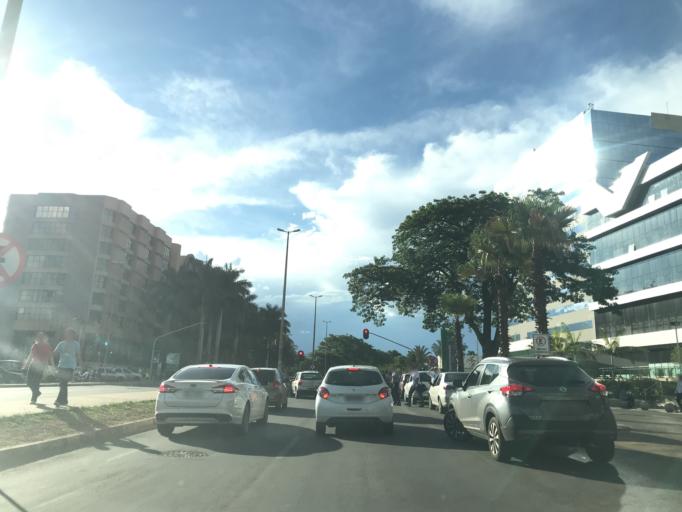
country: BR
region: Federal District
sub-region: Brasilia
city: Brasilia
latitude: -15.7968
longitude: -47.8928
